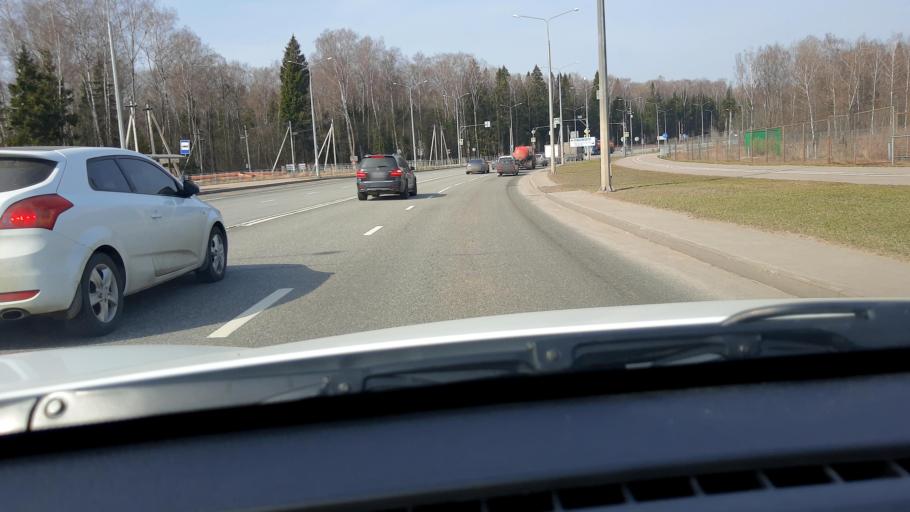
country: RU
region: Moskovskaya
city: Troitsk
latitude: 55.5032
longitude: 37.2693
